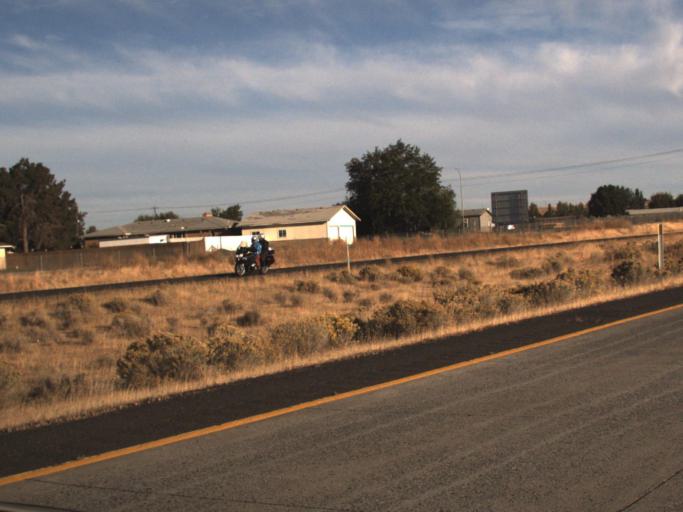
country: US
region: Washington
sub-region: Franklin County
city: Connell
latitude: 46.6585
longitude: -118.8514
